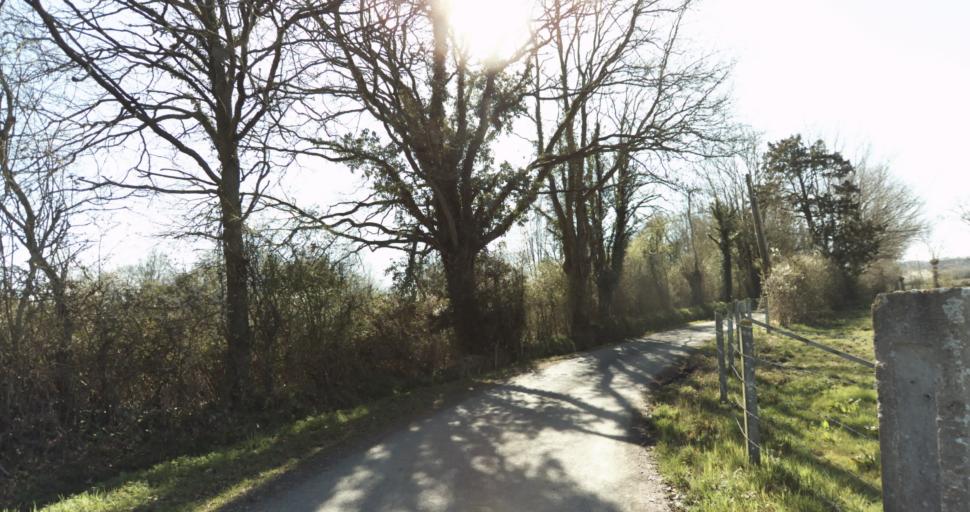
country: FR
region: Lower Normandy
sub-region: Departement du Calvados
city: Livarot
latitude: 48.9905
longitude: 0.0716
